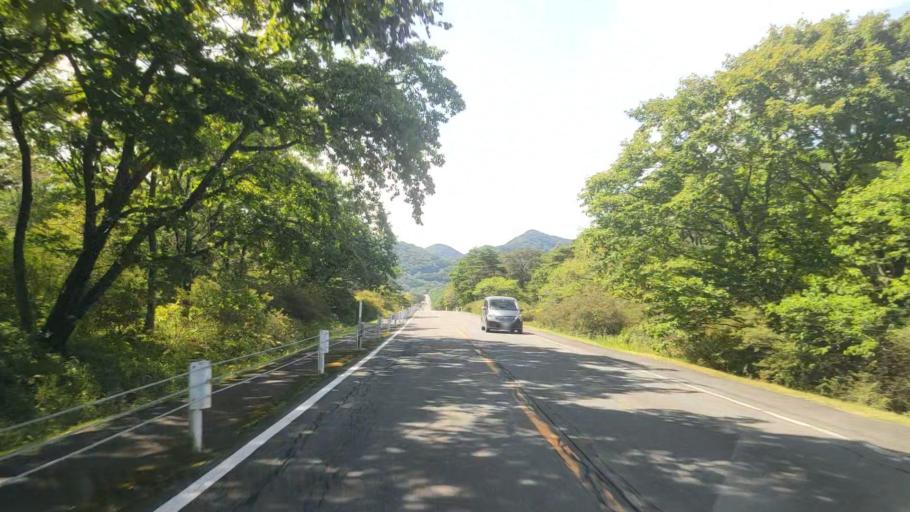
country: JP
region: Gunma
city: Shibukawa
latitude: 36.4795
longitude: 138.8936
